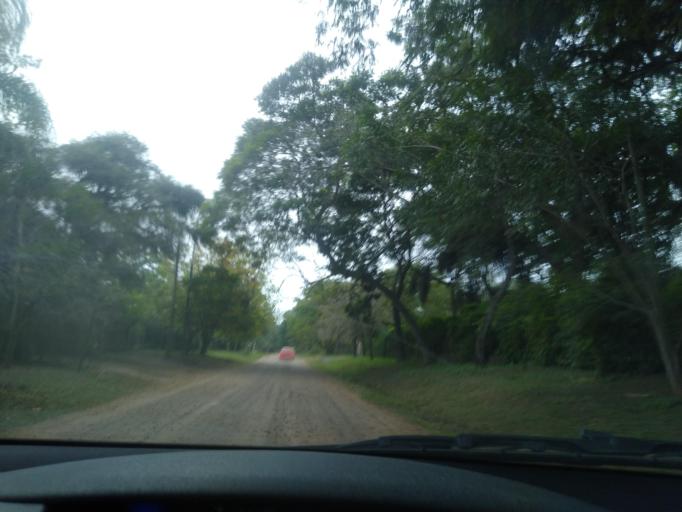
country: AR
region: Chaco
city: Colonia Benitez
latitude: -27.3347
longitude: -58.9559
